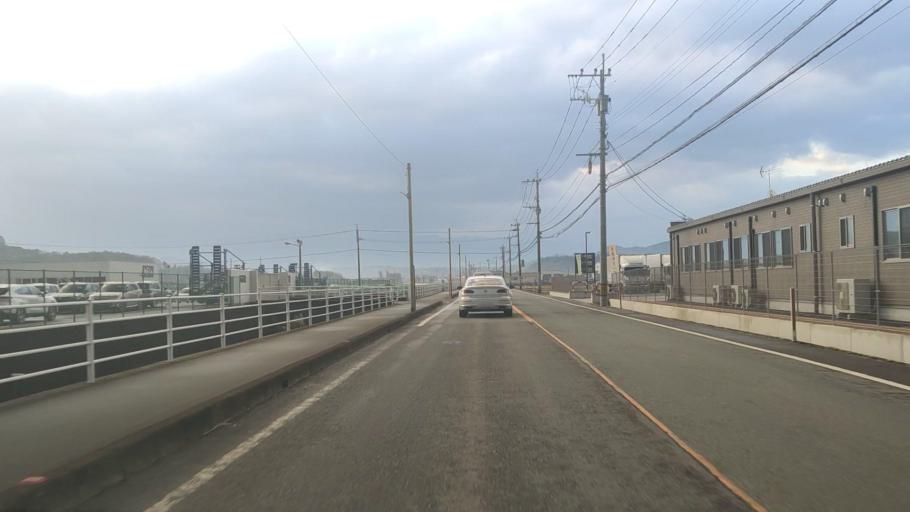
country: JP
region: Kumamoto
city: Uto
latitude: 32.7094
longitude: 130.7757
